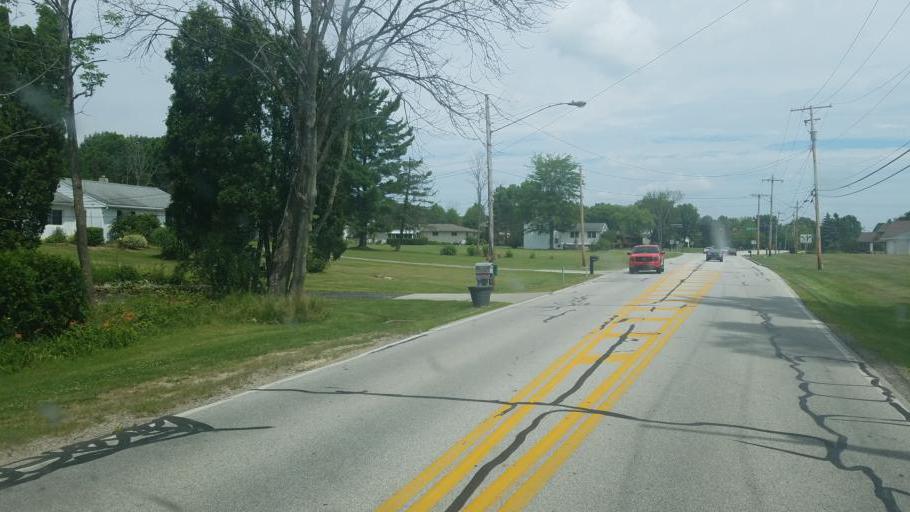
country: US
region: Ohio
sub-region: Cuyahoga County
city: Solon
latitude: 41.3855
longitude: -81.4207
